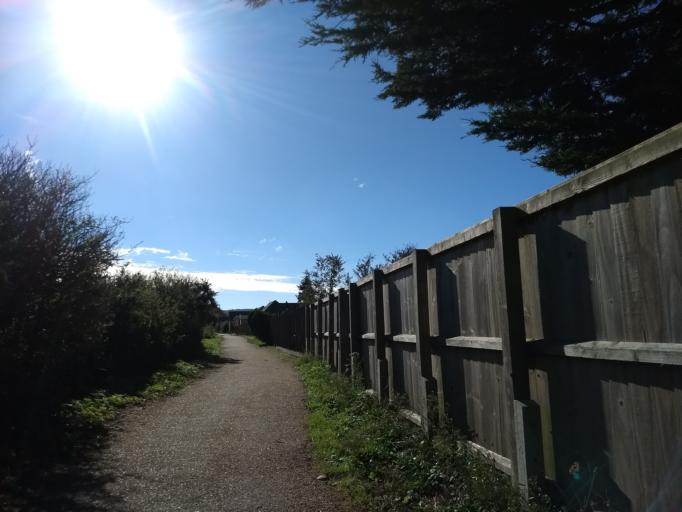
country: GB
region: England
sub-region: Isle of Wight
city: Ventnor
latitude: 50.6215
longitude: -1.2243
